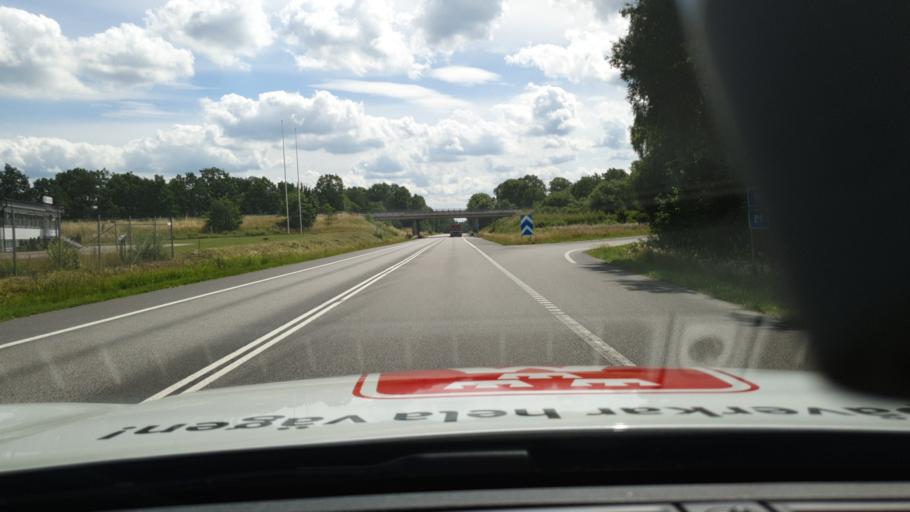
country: SE
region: Skane
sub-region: Hassleholms Kommun
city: Hassleholm
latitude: 56.1416
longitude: 13.8007
